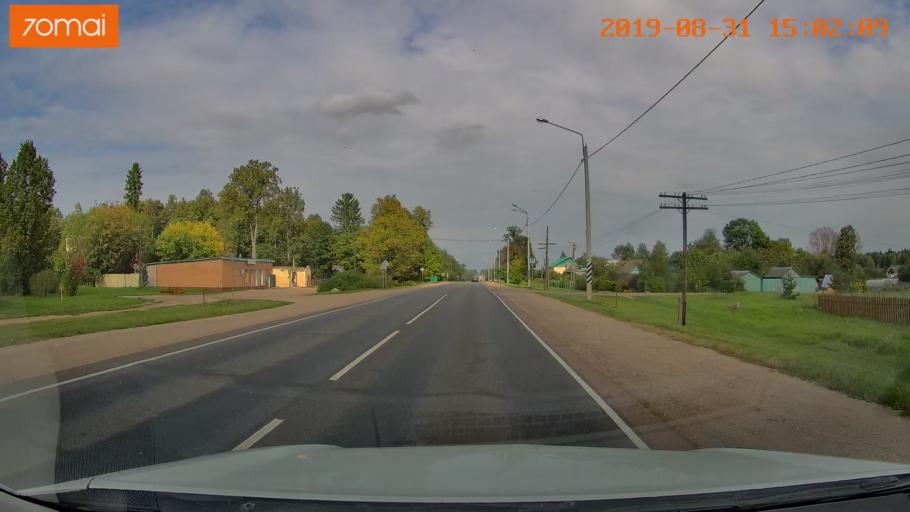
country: RU
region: Kaluga
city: Spas-Demensk
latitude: 54.3438
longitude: 34.0697
